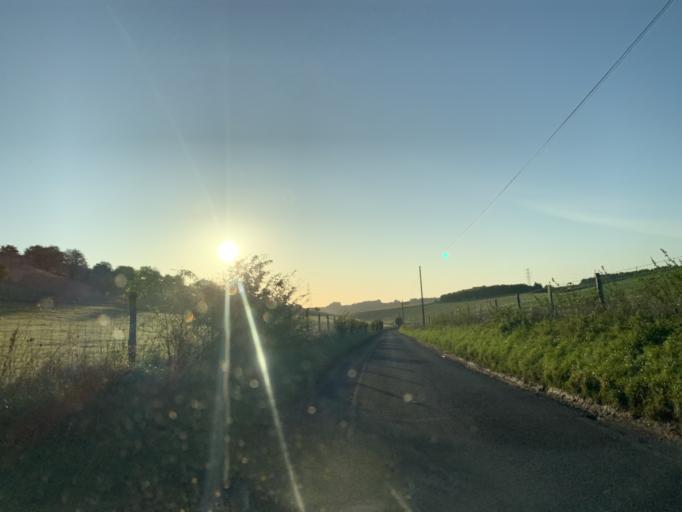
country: GB
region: England
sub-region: Wiltshire
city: Woodford
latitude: 51.1264
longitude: -1.8439
